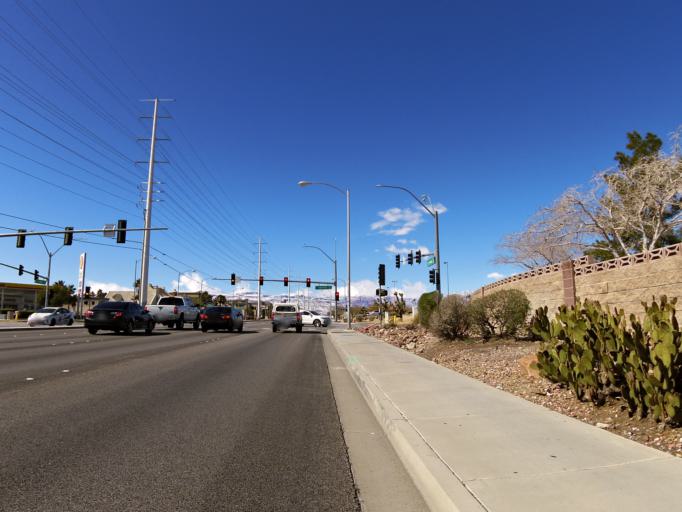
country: US
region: Nevada
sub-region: Clark County
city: Spring Valley
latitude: 36.1148
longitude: -115.2694
